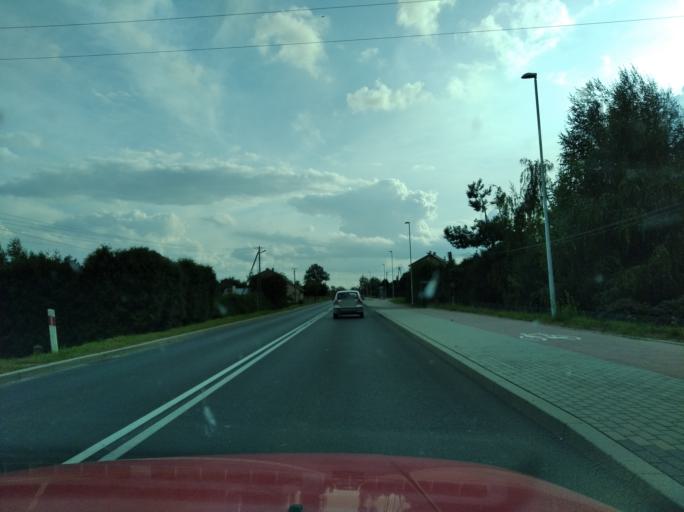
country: PL
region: Subcarpathian Voivodeship
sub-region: Powiat jaroslawski
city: Pawlosiow
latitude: 49.9944
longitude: 22.6656
